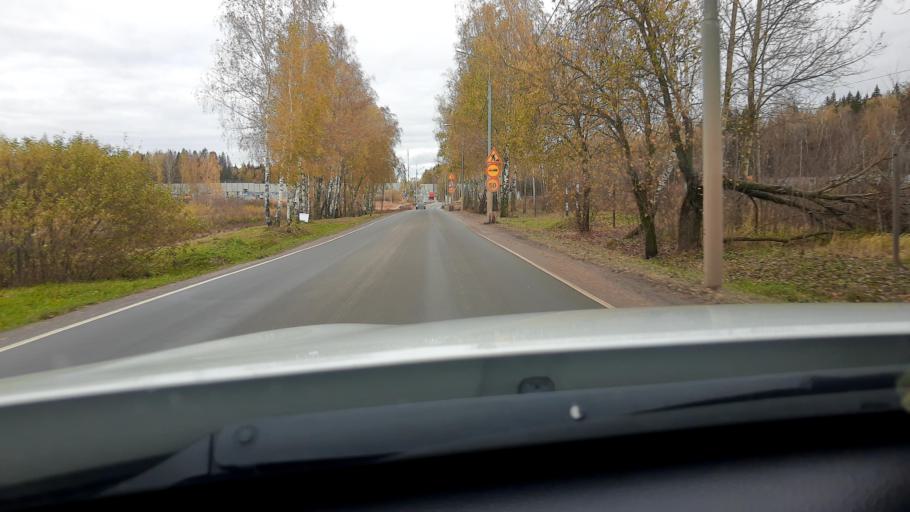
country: RU
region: Moskovskaya
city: Annino
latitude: 55.5753
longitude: 37.2367
